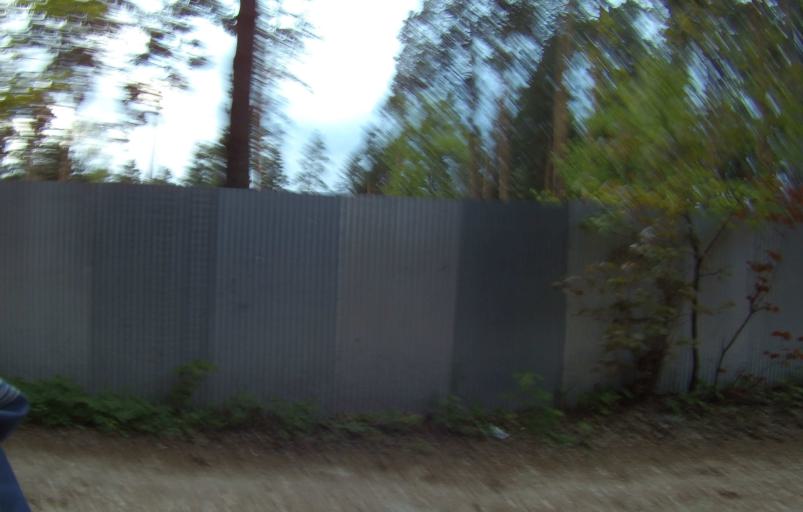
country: RU
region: Moskovskaya
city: Kratovo
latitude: 55.6055
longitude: 38.1563
